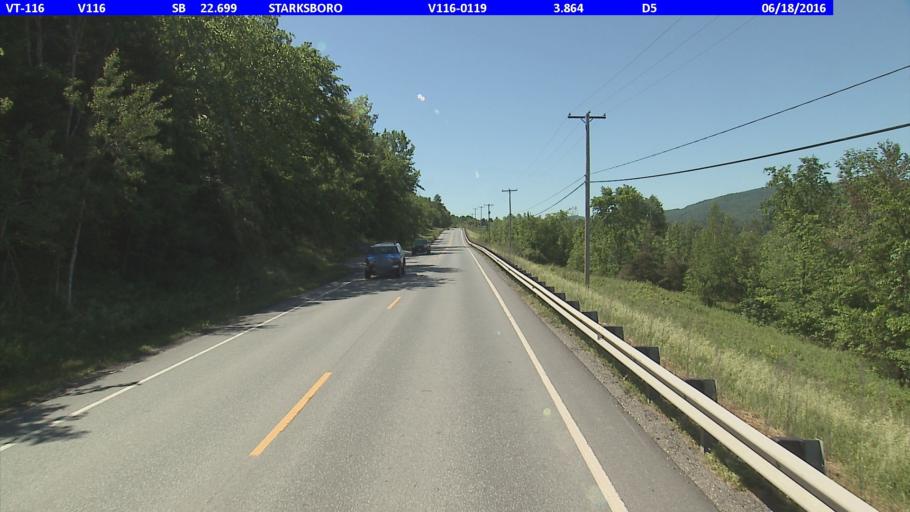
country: US
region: Vermont
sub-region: Chittenden County
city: Hinesburg
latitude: 44.2404
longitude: -73.0582
